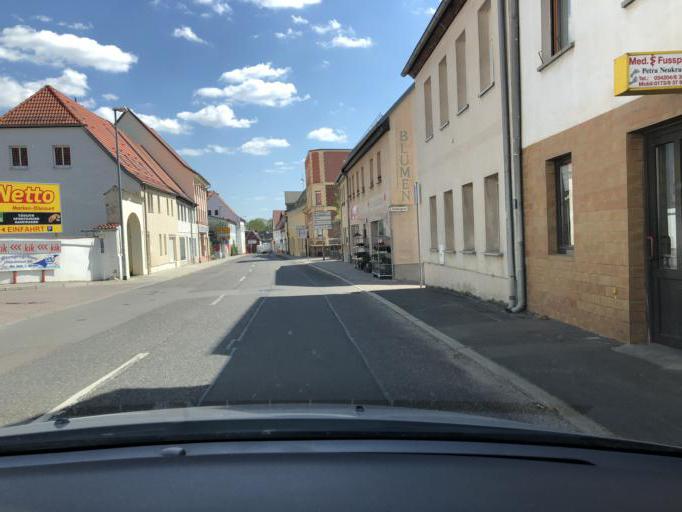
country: DE
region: Saxony
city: Schkeuditz
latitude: 51.3943
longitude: 12.2179
